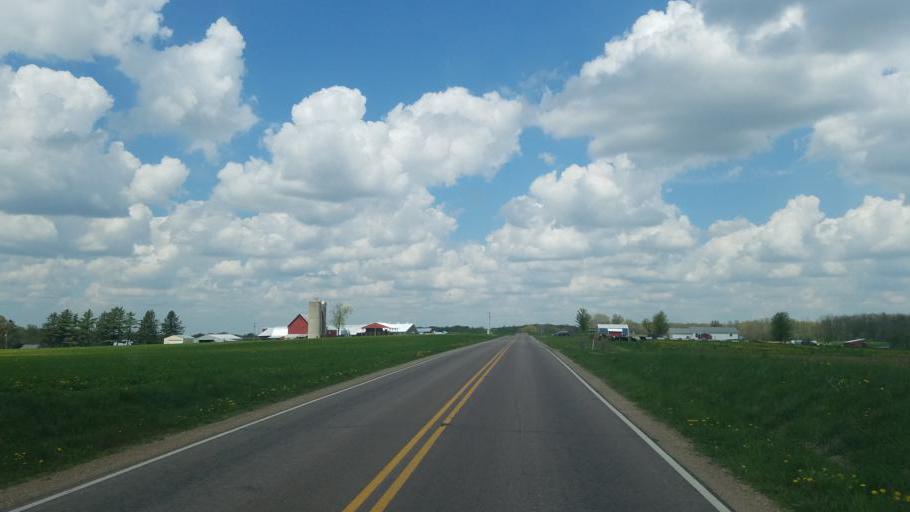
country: US
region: Wisconsin
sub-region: Vernon County
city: Hillsboro
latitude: 43.5978
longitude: -90.3221
